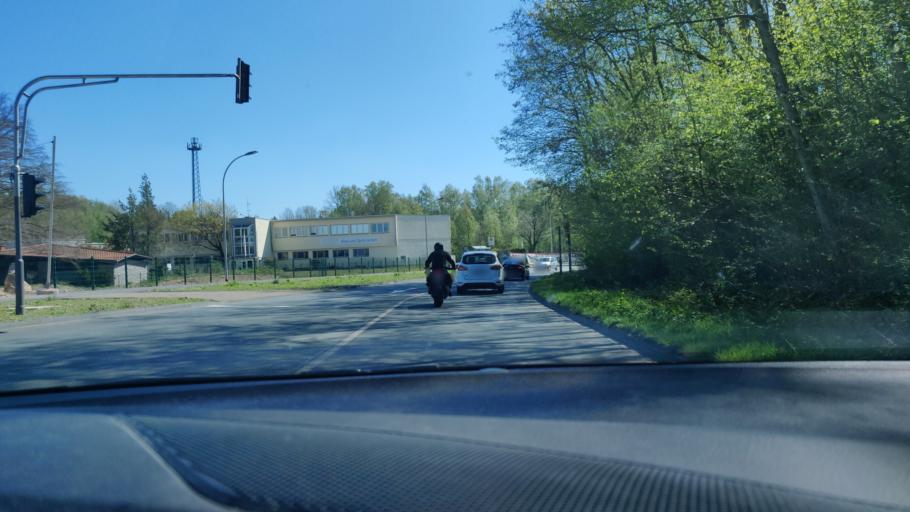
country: DE
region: North Rhine-Westphalia
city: Wulfrath
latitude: 51.2541
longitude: 7.0587
